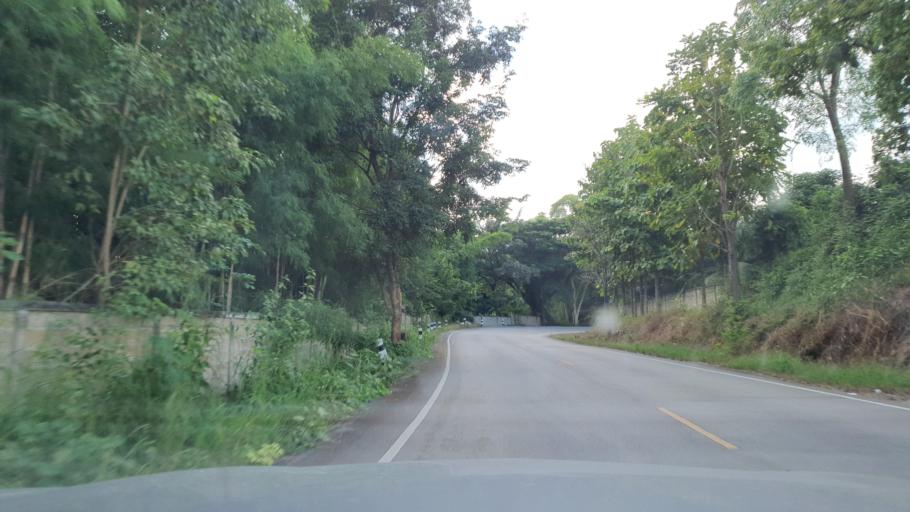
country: TH
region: Phayao
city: Phayao
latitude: 19.0987
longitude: 99.8286
